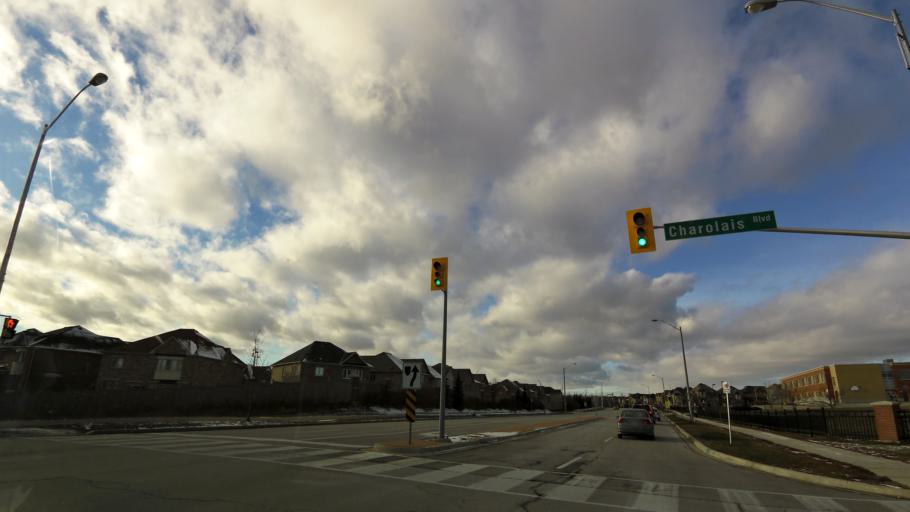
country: CA
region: Ontario
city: Brampton
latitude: 43.6489
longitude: -79.7618
